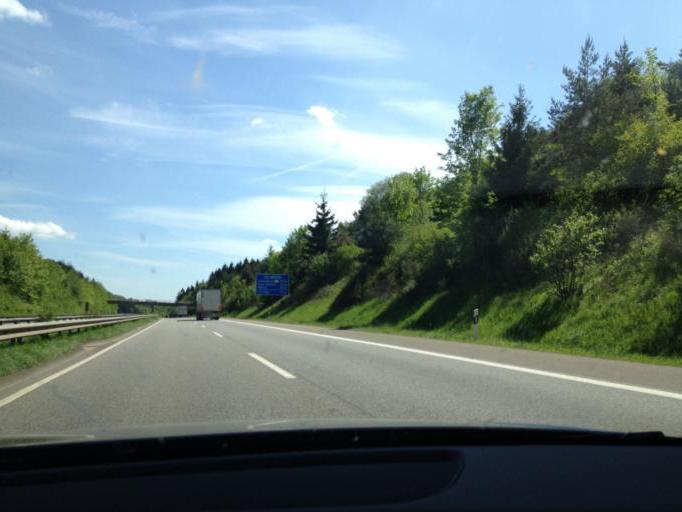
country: DE
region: Rheinland-Pfalz
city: Orlenbach
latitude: 50.1704
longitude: 6.3906
